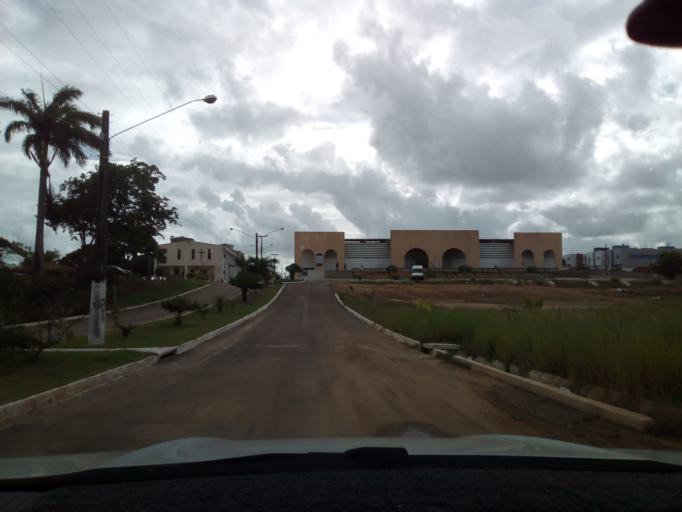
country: BR
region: Paraiba
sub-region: Joao Pessoa
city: Joao Pessoa
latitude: -7.1878
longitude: -34.8745
